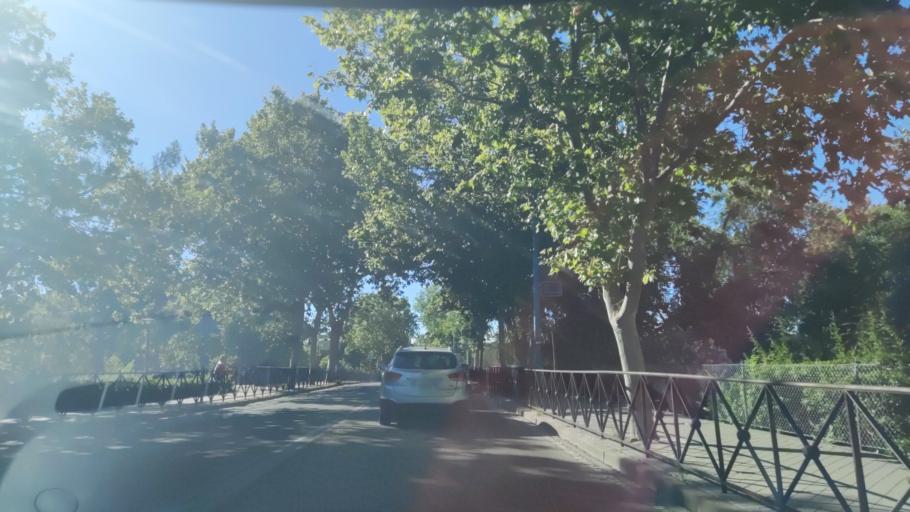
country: ES
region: Madrid
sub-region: Provincia de Madrid
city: Leganes
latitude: 40.3354
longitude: -3.7632
